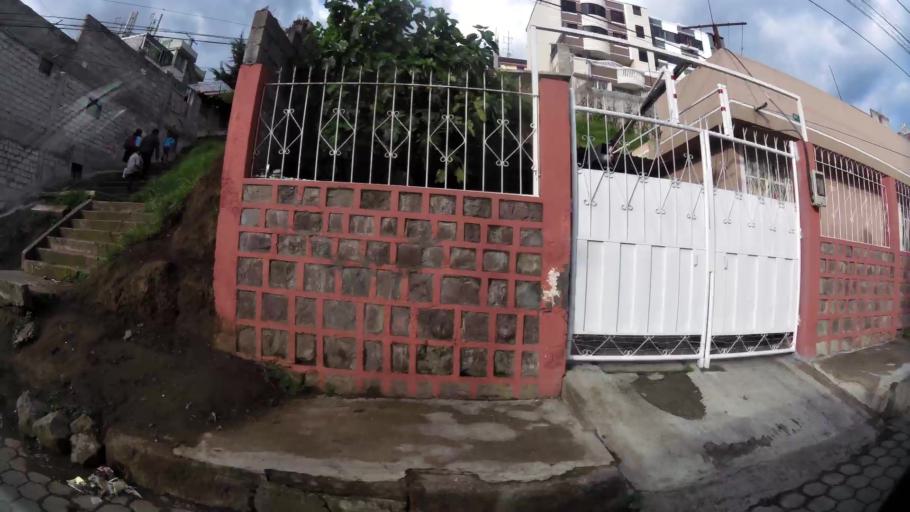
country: EC
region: Pichincha
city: Quito
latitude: -0.1277
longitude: -78.4620
